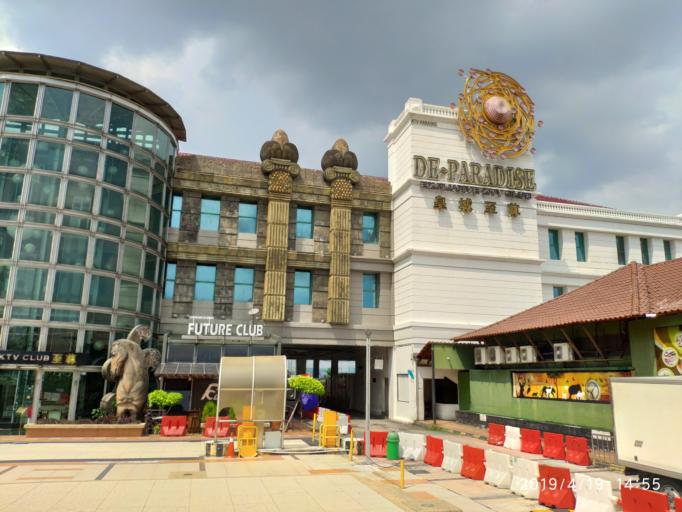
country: MY
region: Johor
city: Johor Bahru
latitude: 1.4709
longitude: 103.7842
